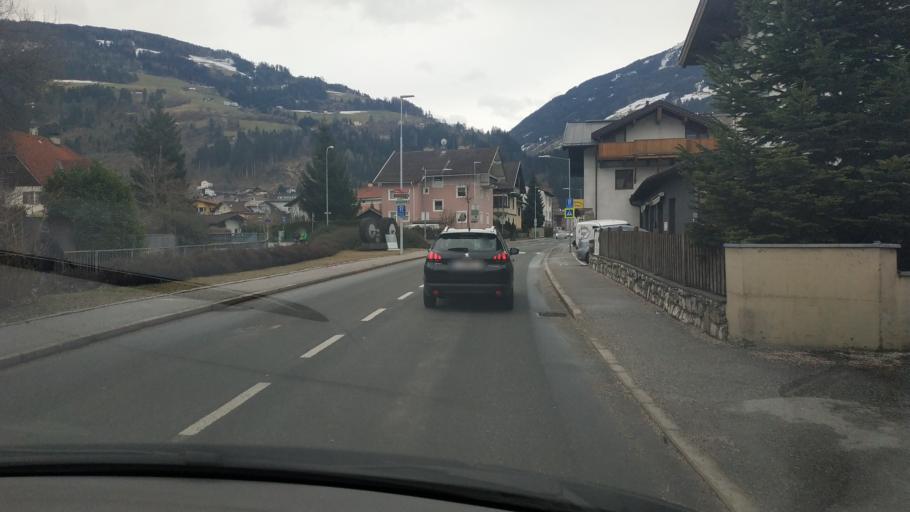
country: AT
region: Tyrol
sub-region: Politischer Bezirk Innsbruck Land
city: Fritzens
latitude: 47.2933
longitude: 11.5902
